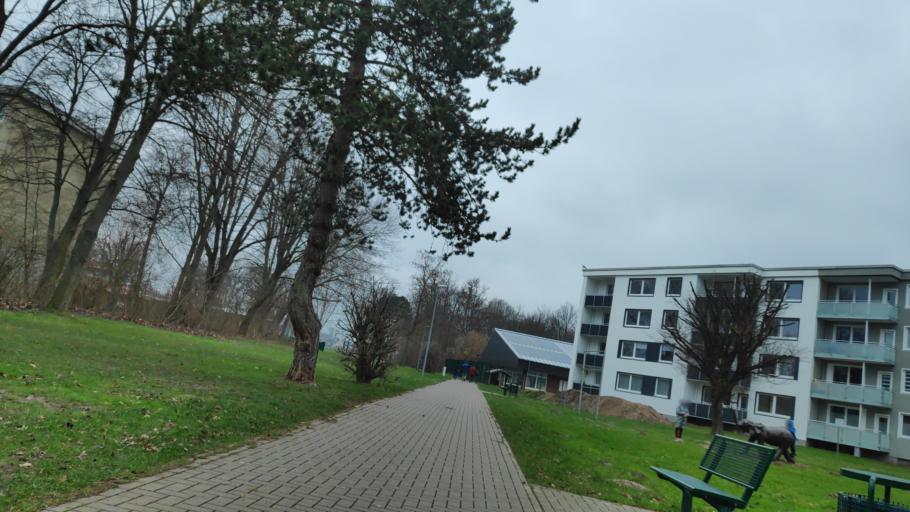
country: DE
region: North Rhine-Westphalia
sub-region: Regierungsbezirk Detmold
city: Minden
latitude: 52.3047
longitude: 8.8883
